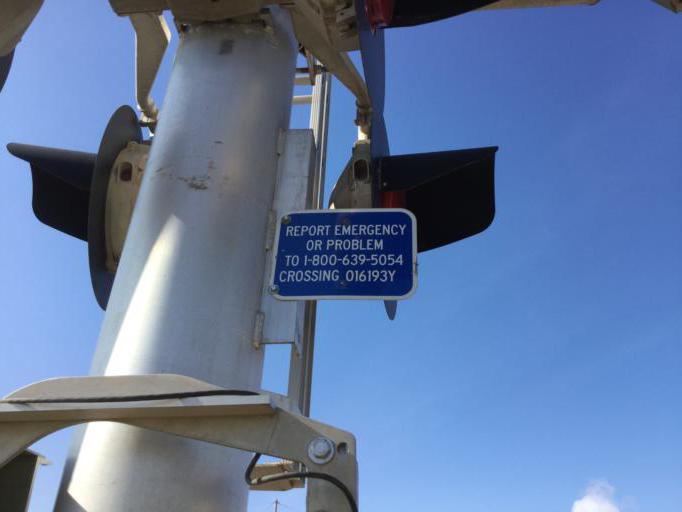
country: US
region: Kansas
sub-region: Barber County
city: Medicine Lodge
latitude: 37.2802
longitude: -98.5867
